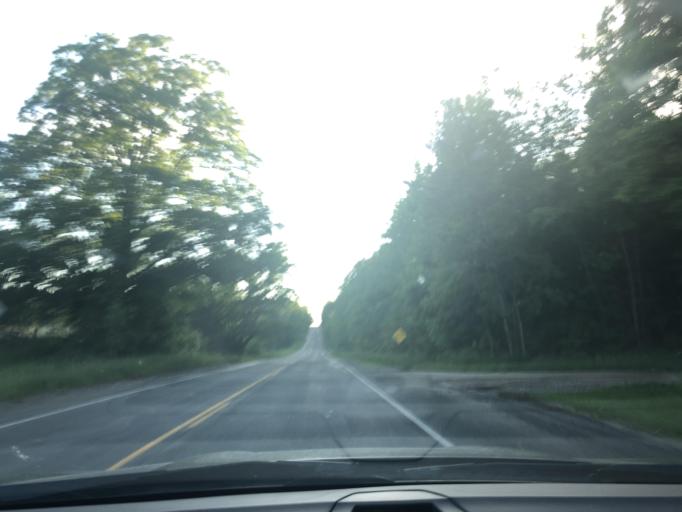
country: US
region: Michigan
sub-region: Missaukee County
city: Lake City
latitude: 44.4669
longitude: -85.1020
